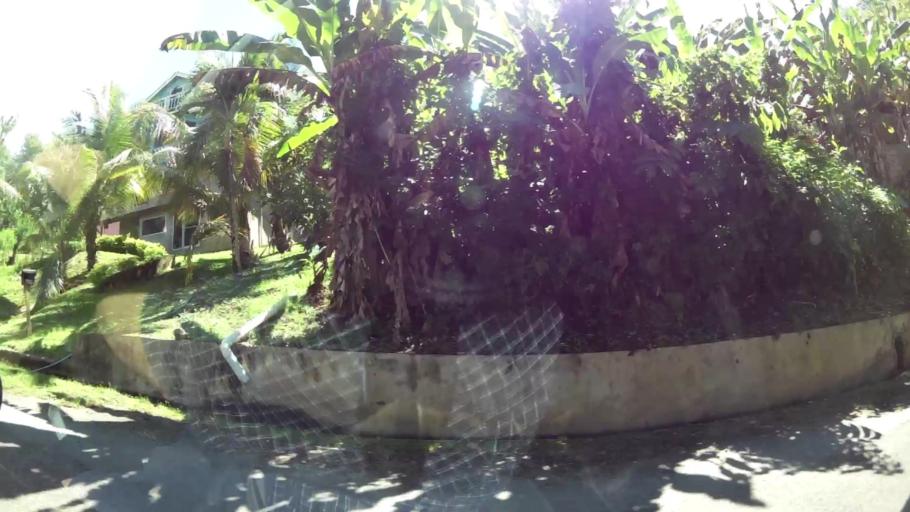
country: TT
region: Tobago
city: Scarborough
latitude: 11.1865
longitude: -60.7798
